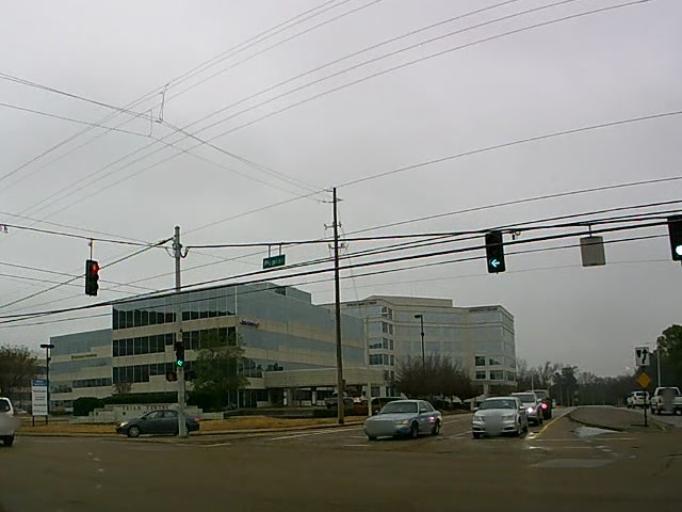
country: US
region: Tennessee
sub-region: Shelby County
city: Germantown
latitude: 35.1020
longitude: -89.8597
